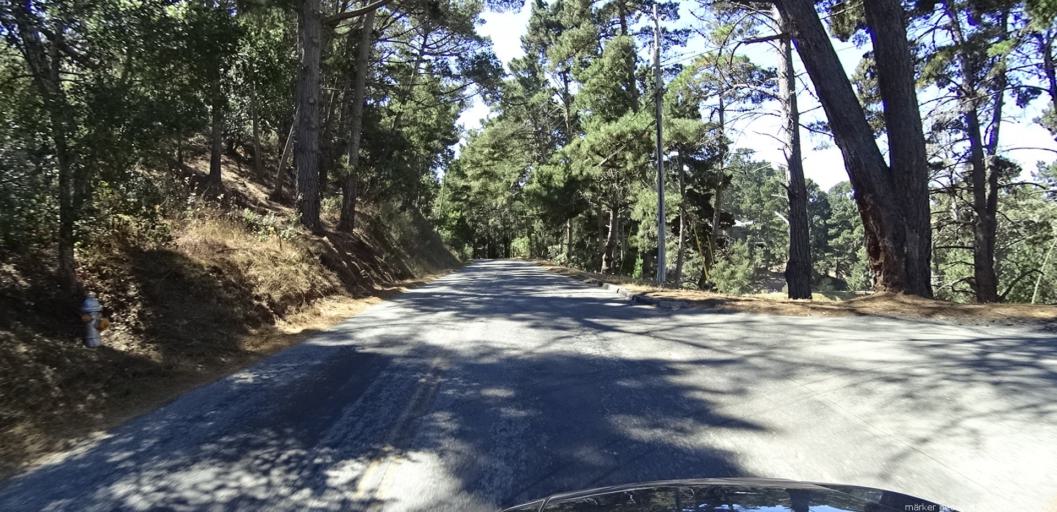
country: US
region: California
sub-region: Monterey County
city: Monterey
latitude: 36.5696
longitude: -121.8929
